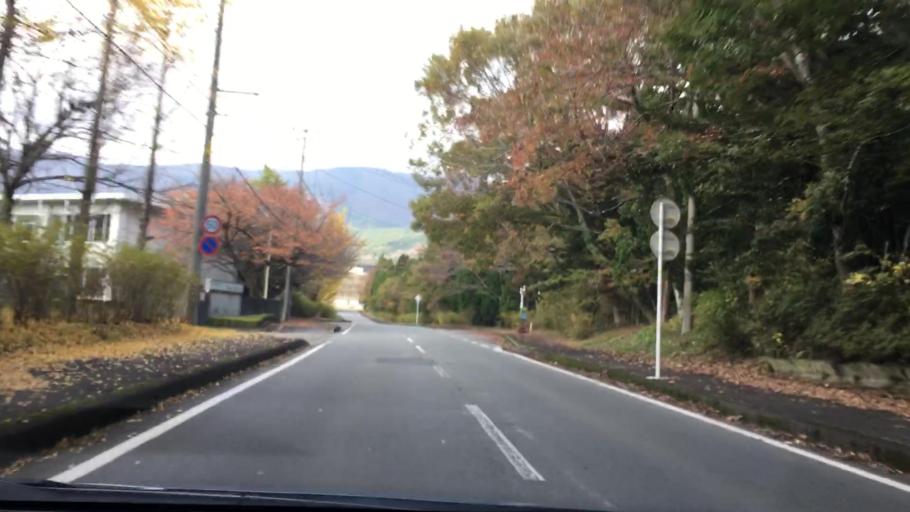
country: JP
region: Shizuoka
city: Gotemba
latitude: 35.3646
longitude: 138.9407
